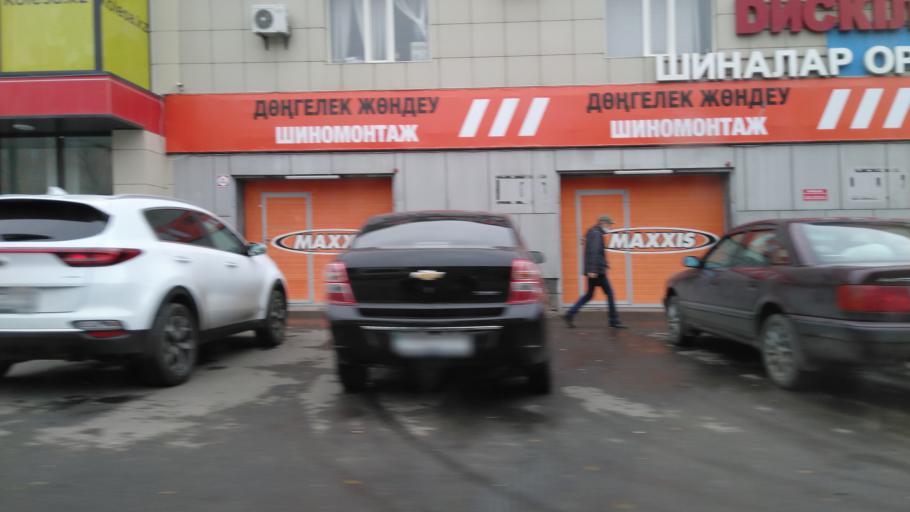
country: KZ
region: Pavlodar
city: Pavlodar
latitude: 52.2778
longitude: 76.9620
